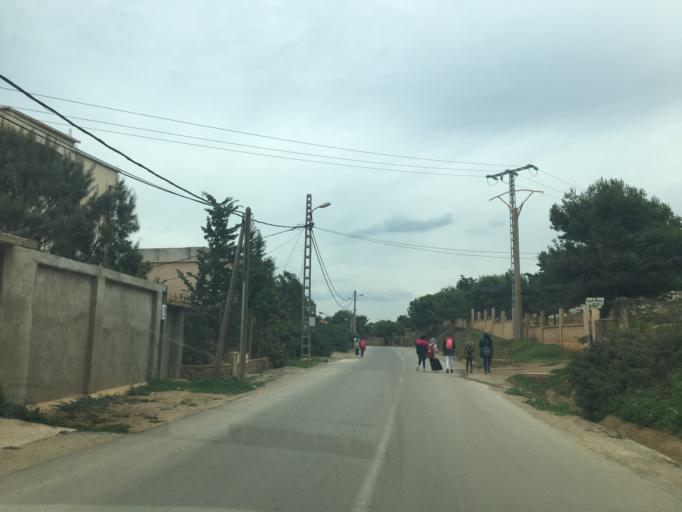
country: DZ
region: Tipaza
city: Tipasa
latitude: 36.6404
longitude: 2.3680
